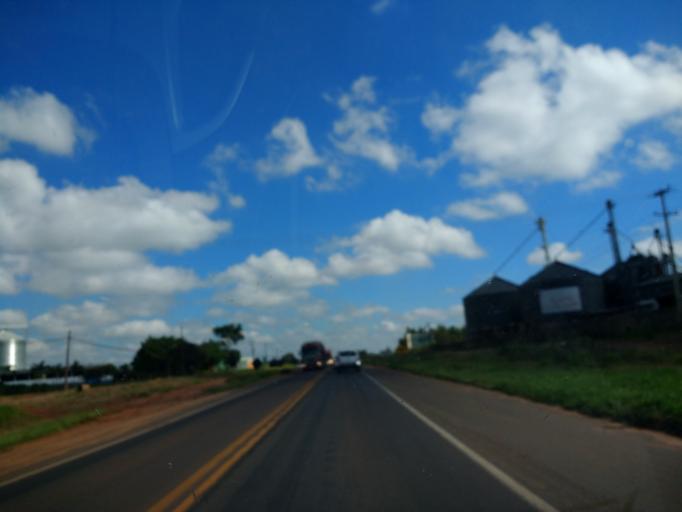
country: BR
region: Parana
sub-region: Umuarama
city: Umuarama
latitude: -23.8112
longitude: -53.3247
